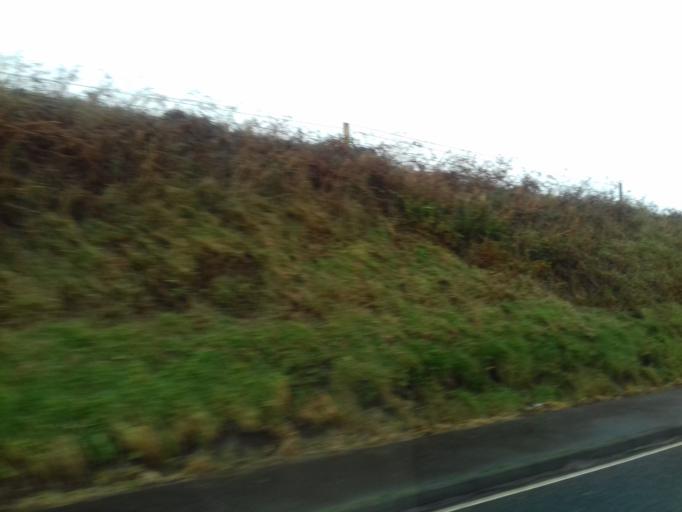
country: GB
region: Northern Ireland
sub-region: Strabane District
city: Sion Mills
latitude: 54.7724
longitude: -7.4657
